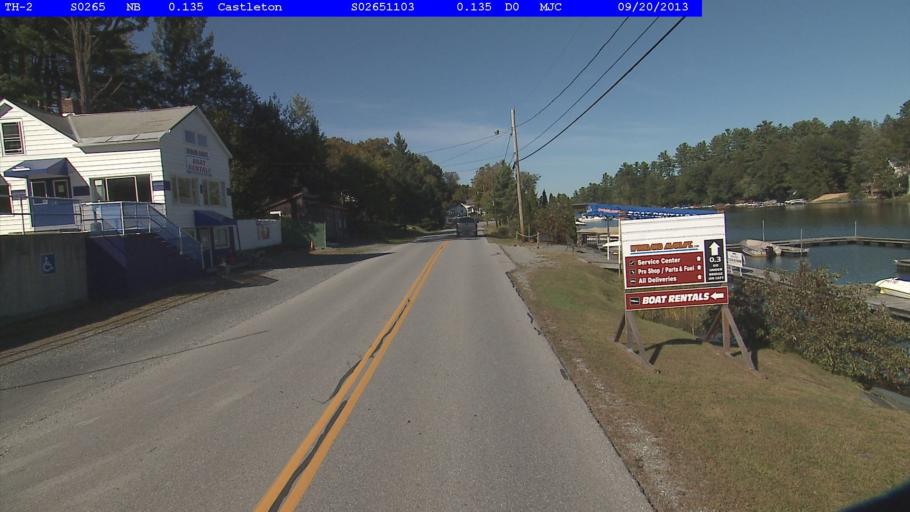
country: US
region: Vermont
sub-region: Rutland County
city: Fair Haven
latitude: 43.6066
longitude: -73.2335
